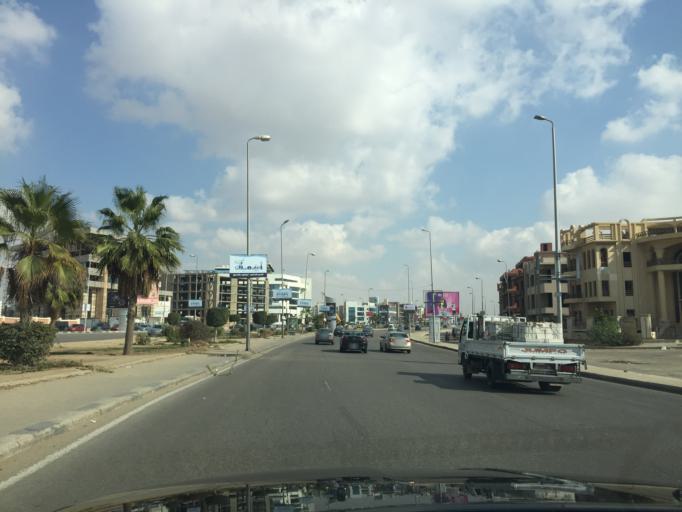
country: EG
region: Muhafazat al Qalyubiyah
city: Al Khankah
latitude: 30.0250
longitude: 31.4565
